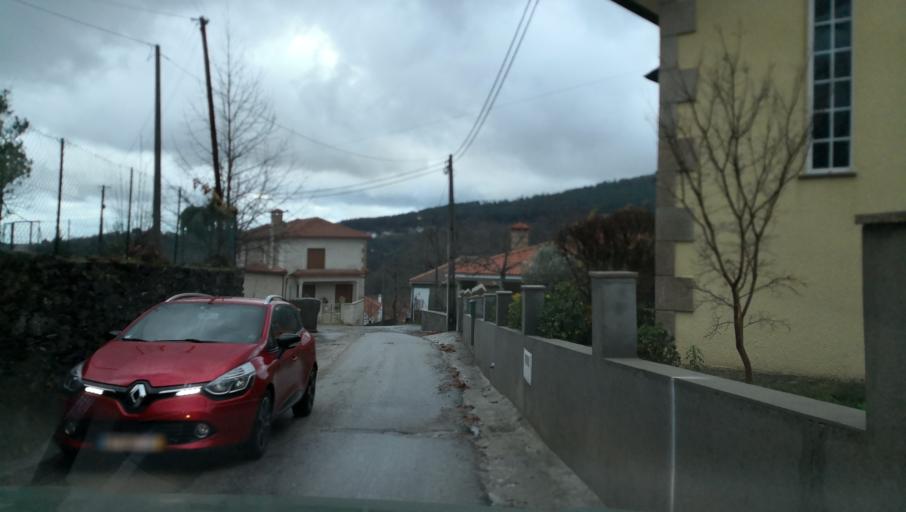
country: PT
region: Vila Real
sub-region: Santa Marta de Penaguiao
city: Santa Marta de Penaguiao
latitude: 41.2928
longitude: -7.8798
